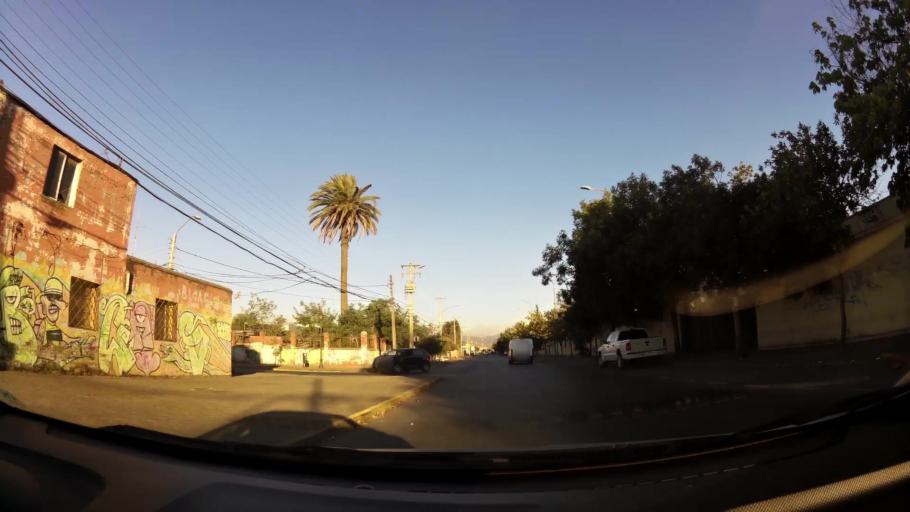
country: CL
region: O'Higgins
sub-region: Provincia de Cachapoal
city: Rancagua
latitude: -34.1732
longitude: -70.7525
